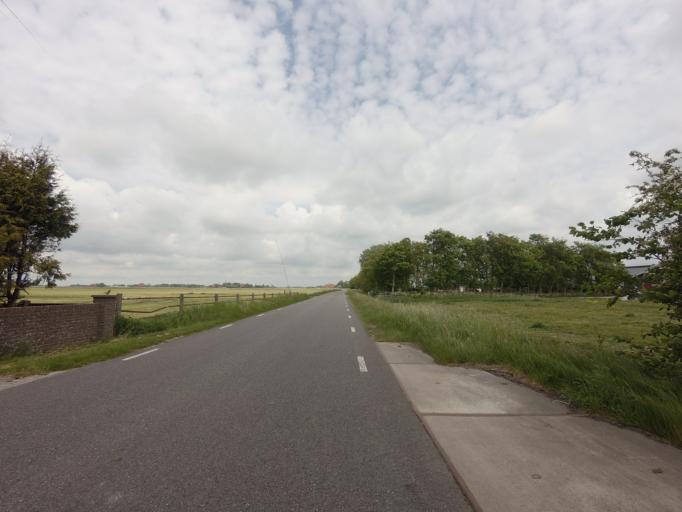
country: NL
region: Friesland
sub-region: Sudwest Fryslan
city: Bolsward
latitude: 53.0989
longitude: 5.5360
